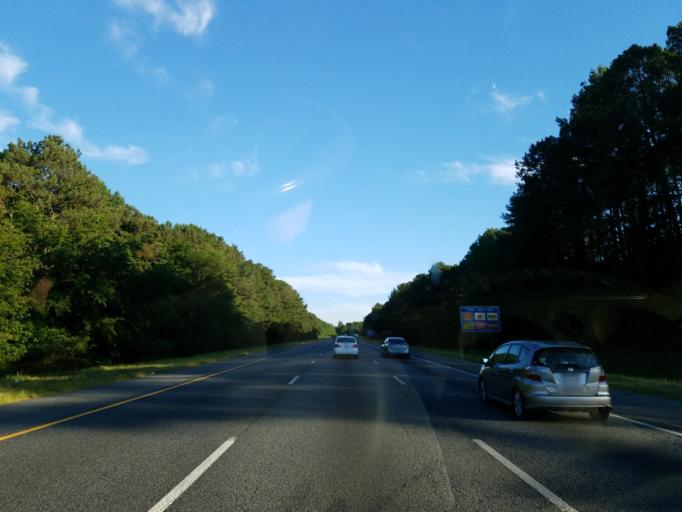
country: US
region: Georgia
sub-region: Bartow County
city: Cartersville
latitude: 34.2254
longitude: -84.7534
